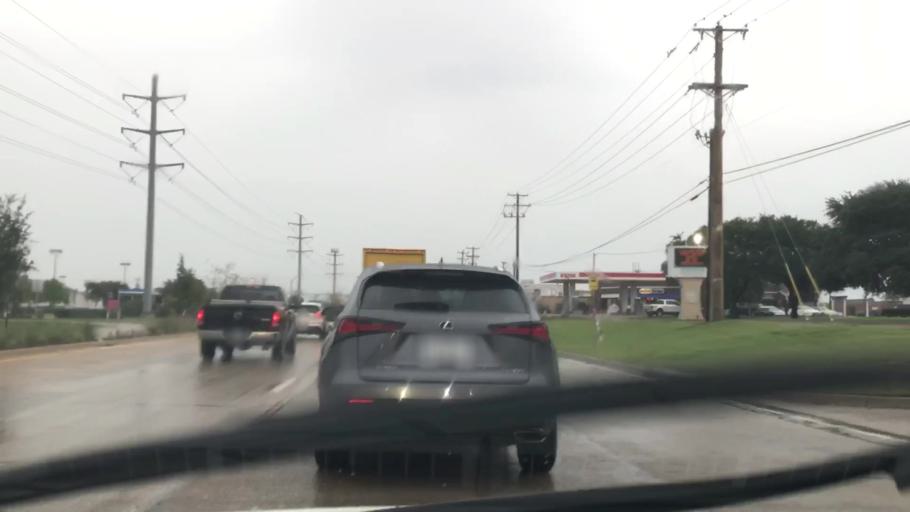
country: US
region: Texas
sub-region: Dallas County
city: Rowlett
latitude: 32.9162
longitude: -96.5200
